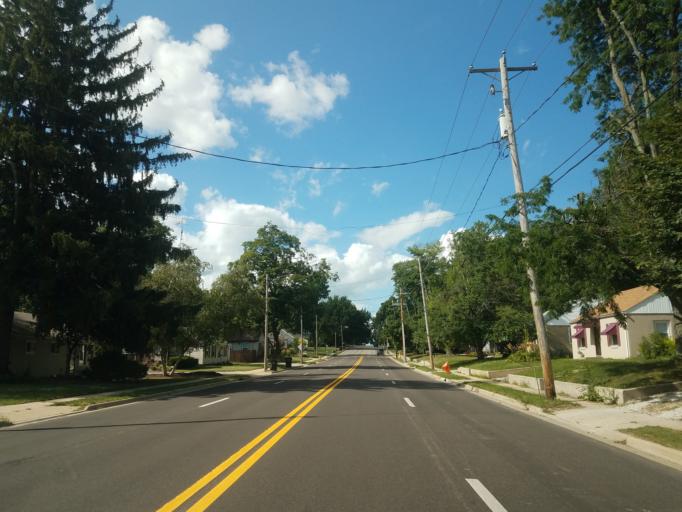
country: US
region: Illinois
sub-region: McLean County
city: Bloomington
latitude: 40.4945
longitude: -88.9820
